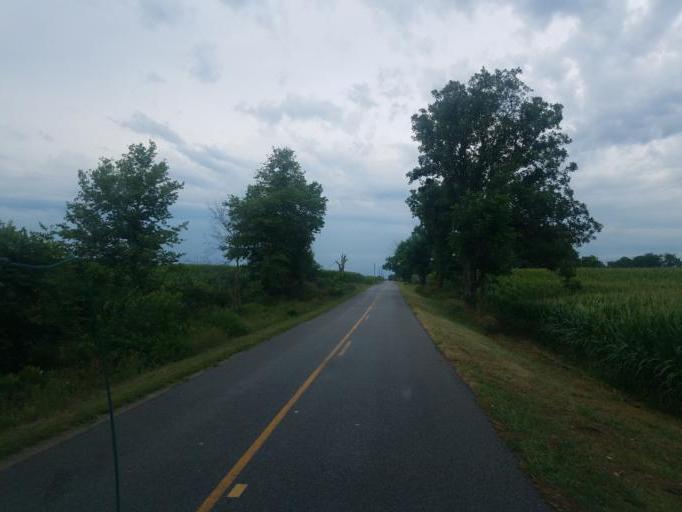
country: US
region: Ohio
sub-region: Paulding County
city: Antwerp
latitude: 41.2374
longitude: -84.7234
